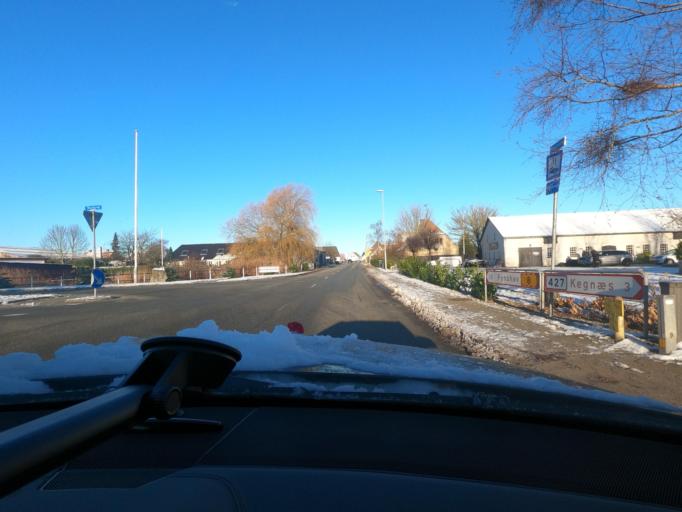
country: DK
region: South Denmark
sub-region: Sonderborg Kommune
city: Horuphav
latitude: 54.8828
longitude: 9.9955
